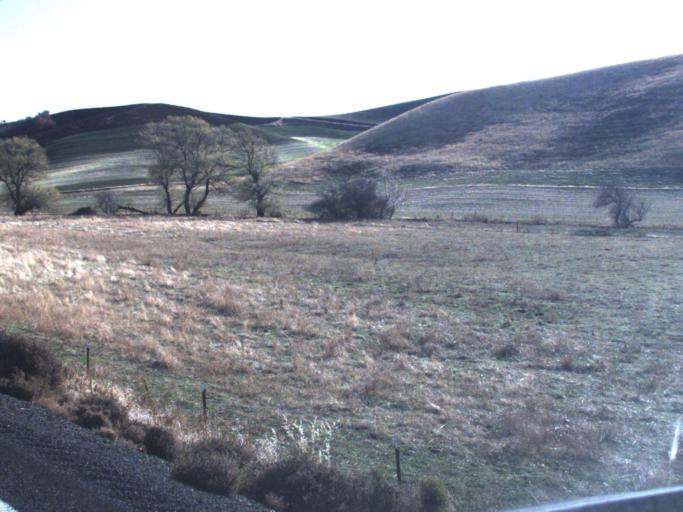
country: US
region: Washington
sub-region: Whitman County
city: Colfax
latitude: 46.7582
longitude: -117.4500
